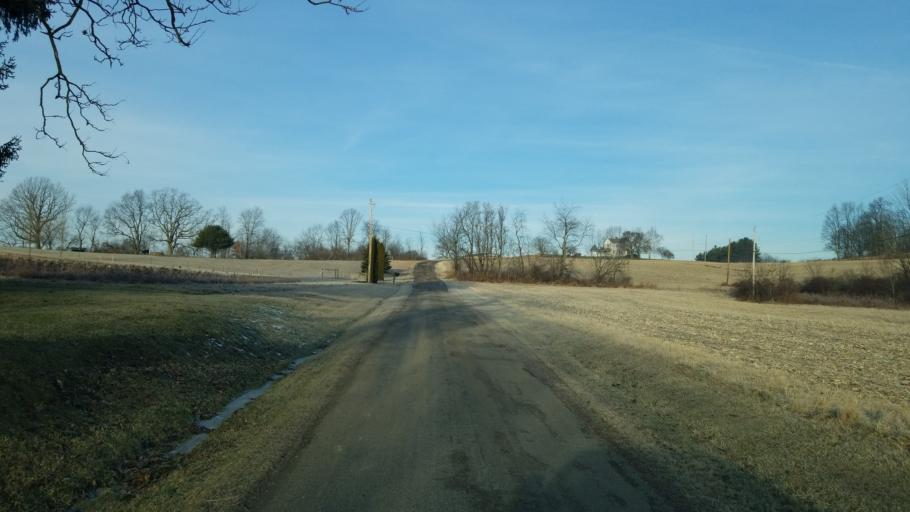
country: US
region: Pennsylvania
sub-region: Indiana County
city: Chevy Chase Heights
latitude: 40.8465
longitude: -79.2597
